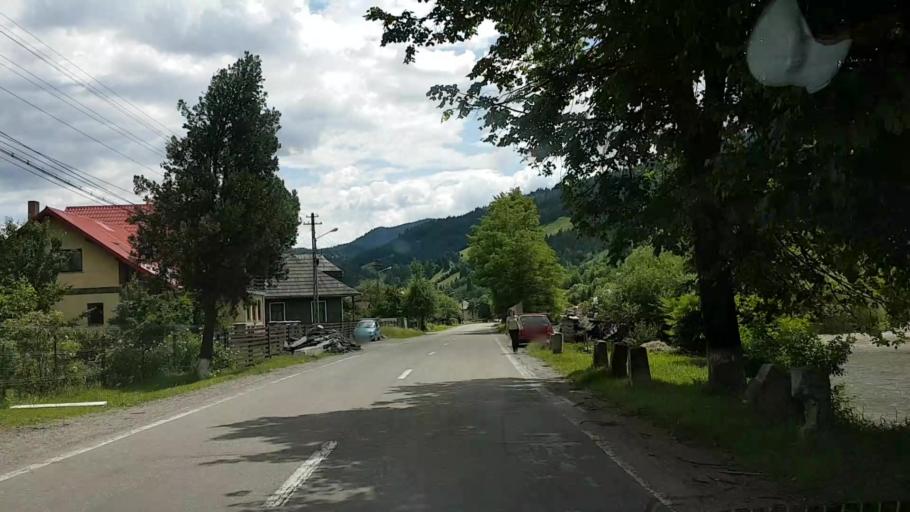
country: RO
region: Suceava
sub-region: Comuna Brosteni
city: Brosteni
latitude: 47.2395
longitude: 25.7092
